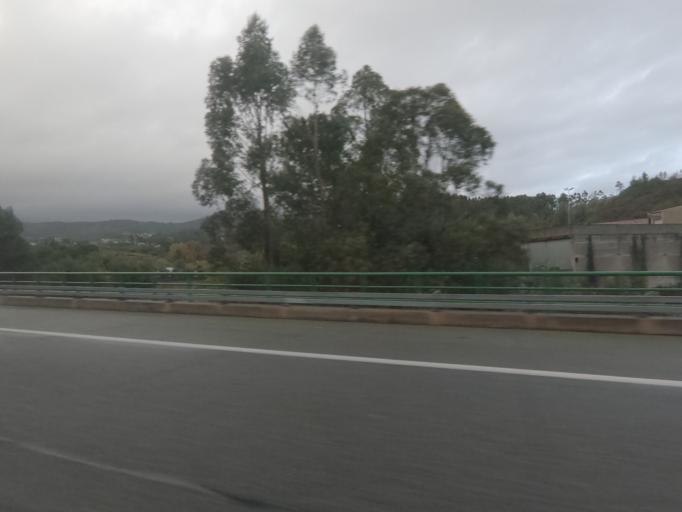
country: PT
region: Viana do Castelo
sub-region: Ponte de Lima
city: Ponte de Lima
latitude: 41.7852
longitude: -8.5736
